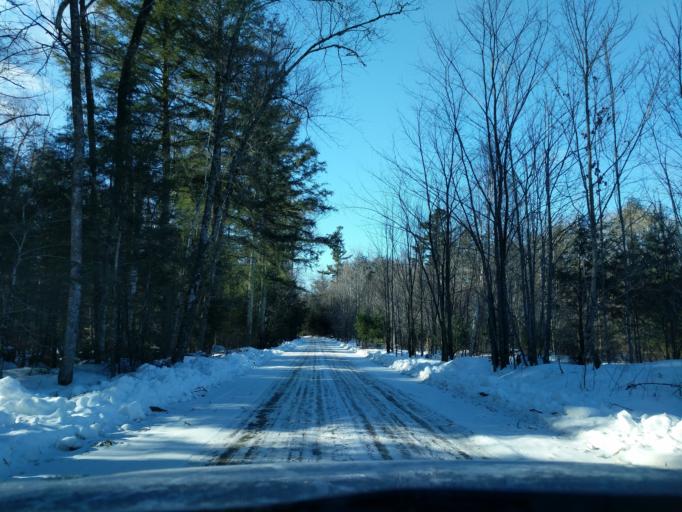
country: US
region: Wisconsin
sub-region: Menominee County
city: Keshena
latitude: 45.0981
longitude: -88.6094
